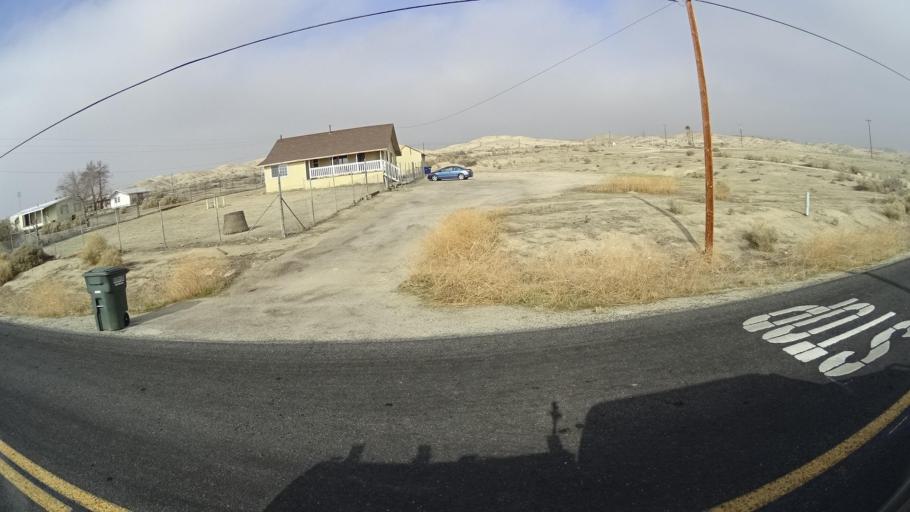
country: US
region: California
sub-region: Kern County
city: Ford City
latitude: 35.2321
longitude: -119.3686
